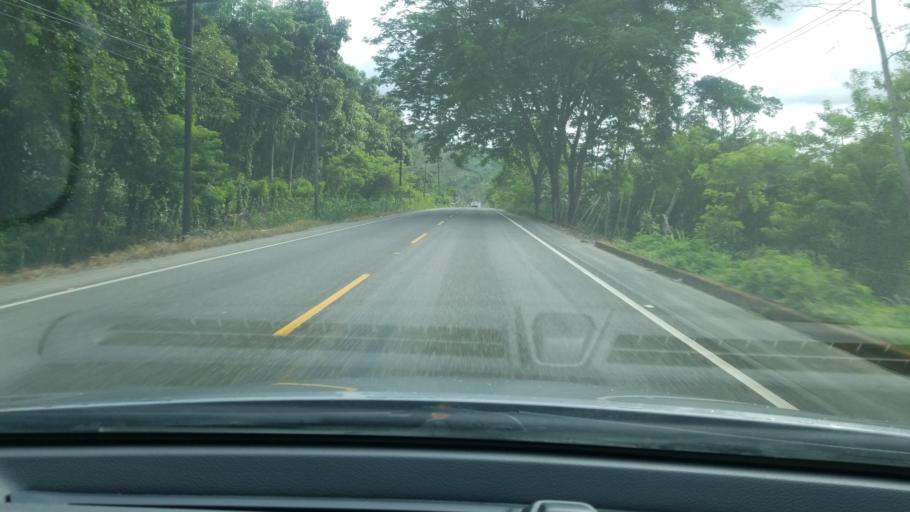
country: HN
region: Cortes
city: Potrerillos
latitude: 15.5949
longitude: -88.3045
